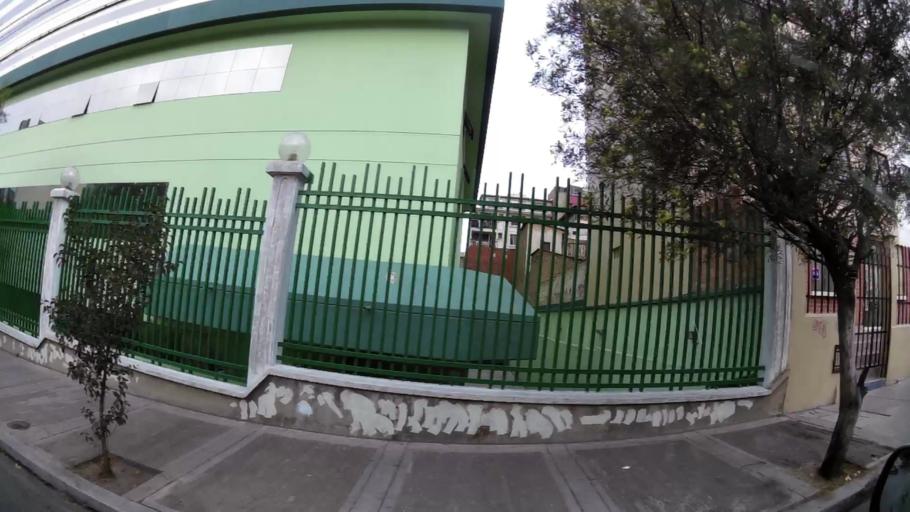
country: BO
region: La Paz
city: La Paz
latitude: -16.5015
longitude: -68.1175
